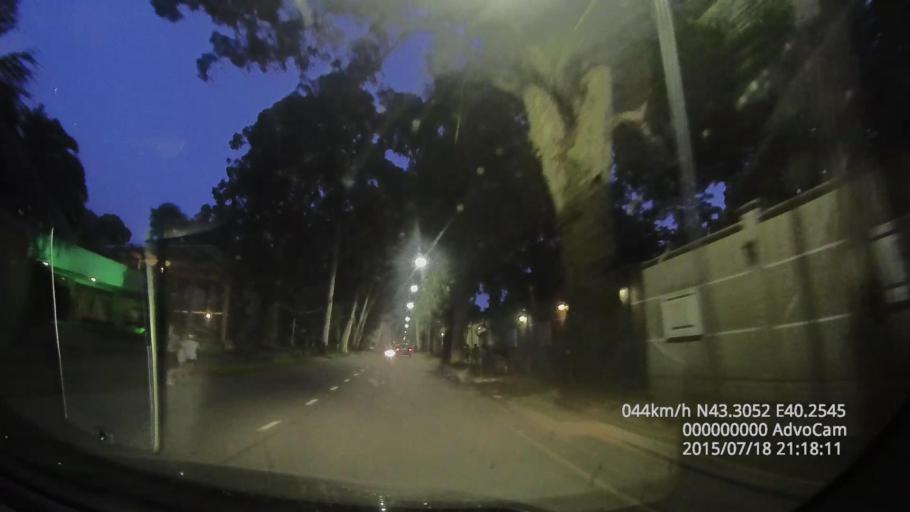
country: GE
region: Abkhazia
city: Gagra
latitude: 43.3050
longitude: 40.2547
